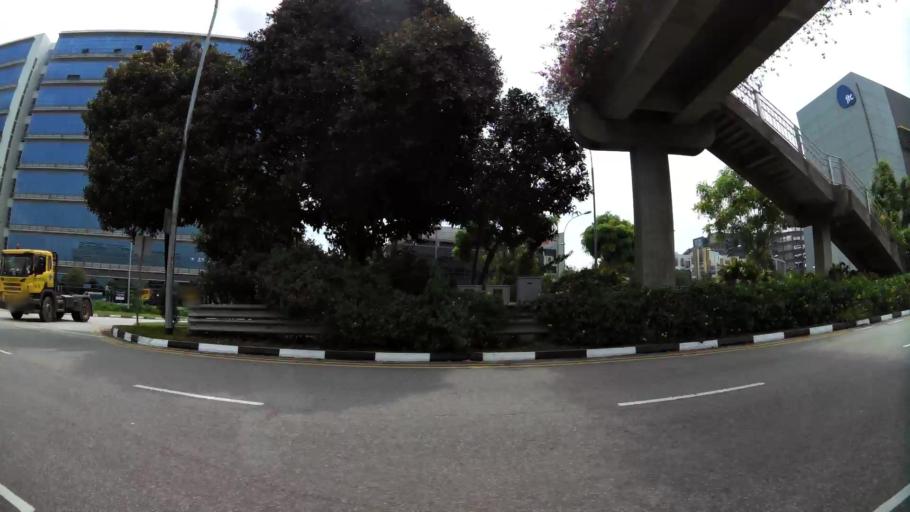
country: SG
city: Singapore
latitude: 1.3136
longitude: 103.7016
